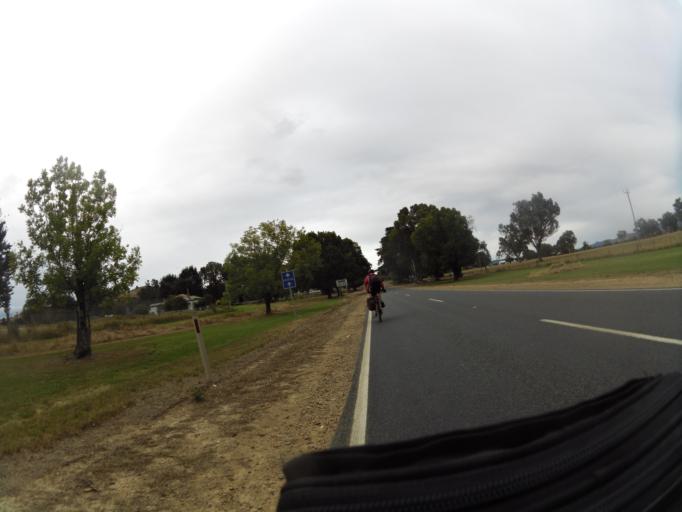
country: AU
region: New South Wales
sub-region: Snowy River
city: Jindabyne
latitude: -36.1852
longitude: 147.9196
